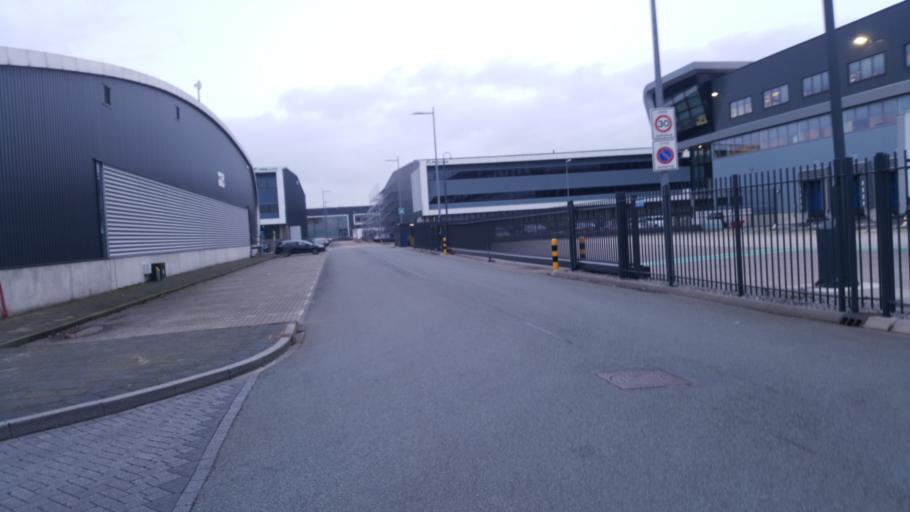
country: NL
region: North Holland
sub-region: Gemeente Aalsmeer
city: Aalsmeer
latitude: 52.2933
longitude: 4.7884
